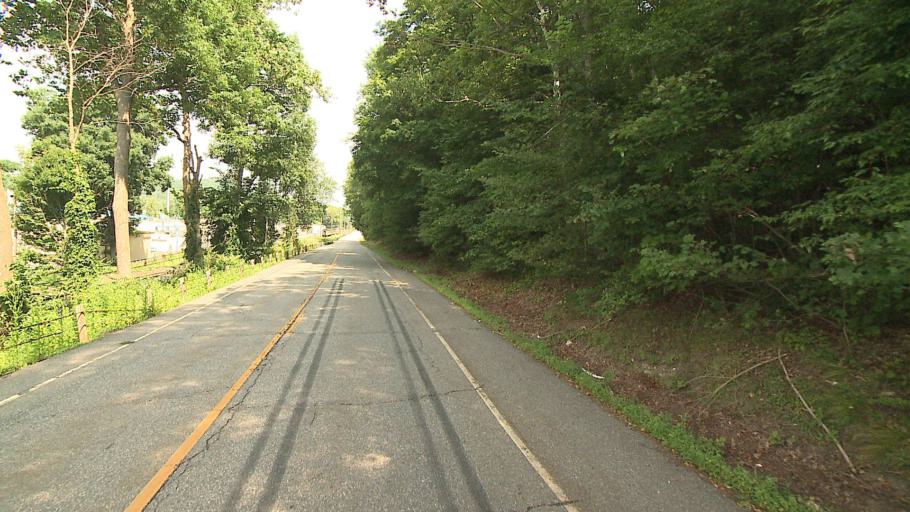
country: US
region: Connecticut
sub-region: Litchfield County
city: Thomaston
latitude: 41.6418
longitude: -73.0780
